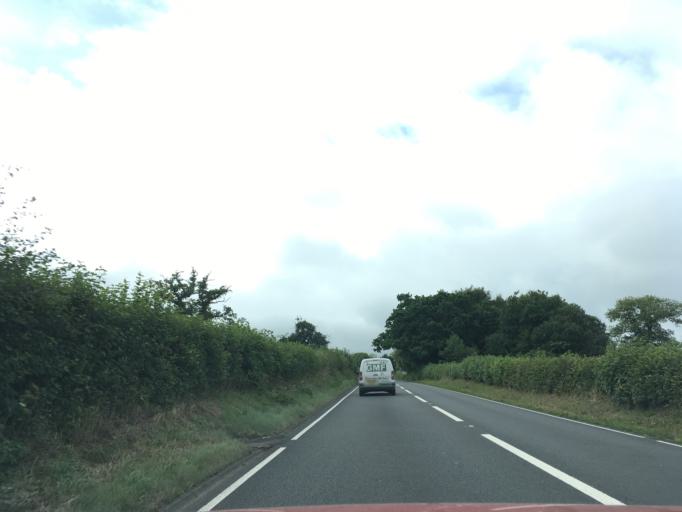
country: GB
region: Wales
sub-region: Carmarthenshire
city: Llanddarog
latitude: 51.8731
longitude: -4.1491
